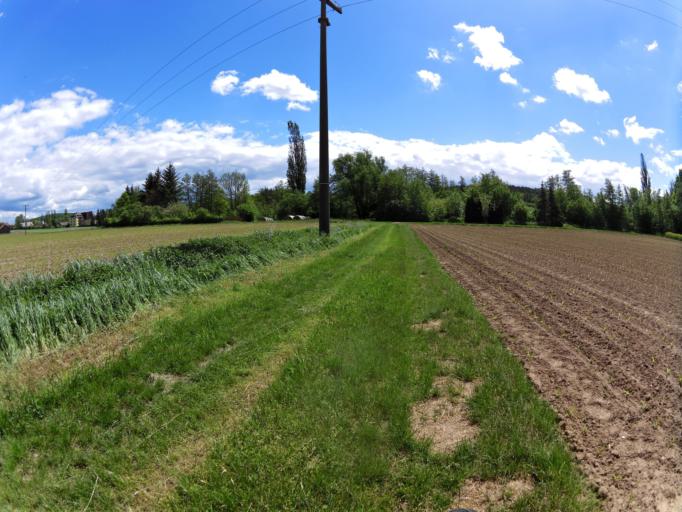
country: DE
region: Bavaria
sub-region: Regierungsbezirk Unterfranken
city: Volkach
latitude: 49.8725
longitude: 10.2481
